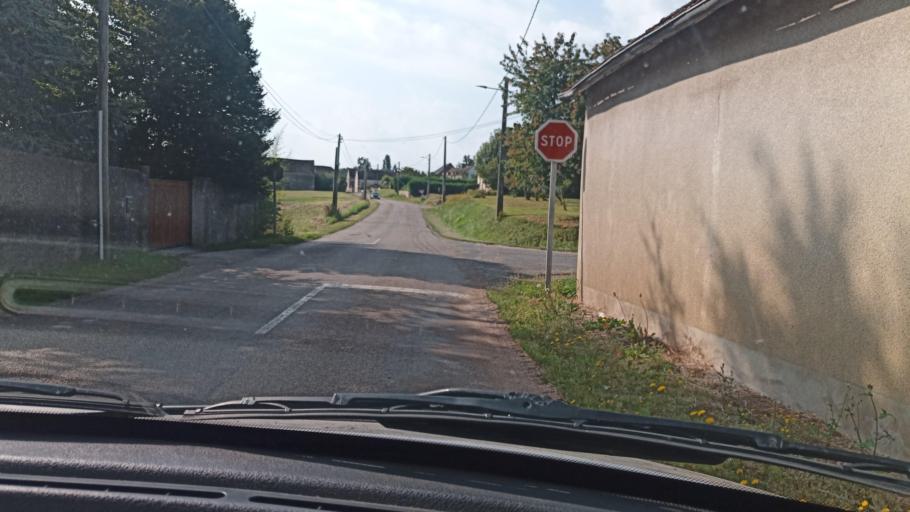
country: FR
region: Bourgogne
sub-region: Departement de l'Yonne
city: Saint-Valerien
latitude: 48.2138
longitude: 3.0716
